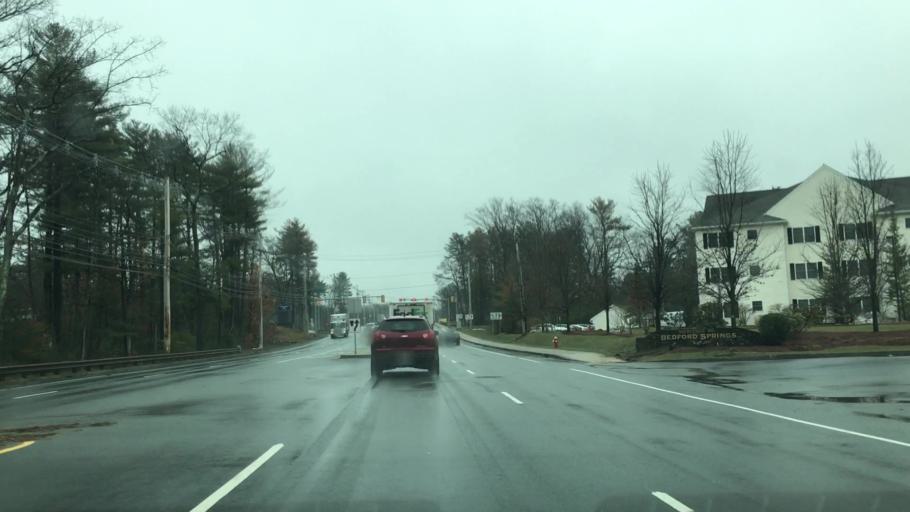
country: US
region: Massachusetts
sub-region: Middlesex County
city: Pinehurst
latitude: 42.5115
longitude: -71.2374
